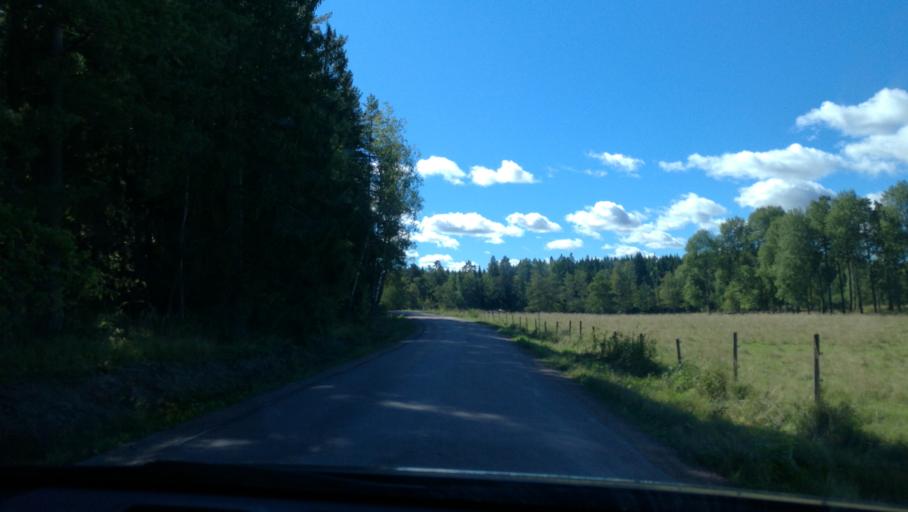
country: SE
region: Vaestmanland
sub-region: Hallstahammars Kommun
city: Hallstahammar
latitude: 59.6530
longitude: 16.1994
